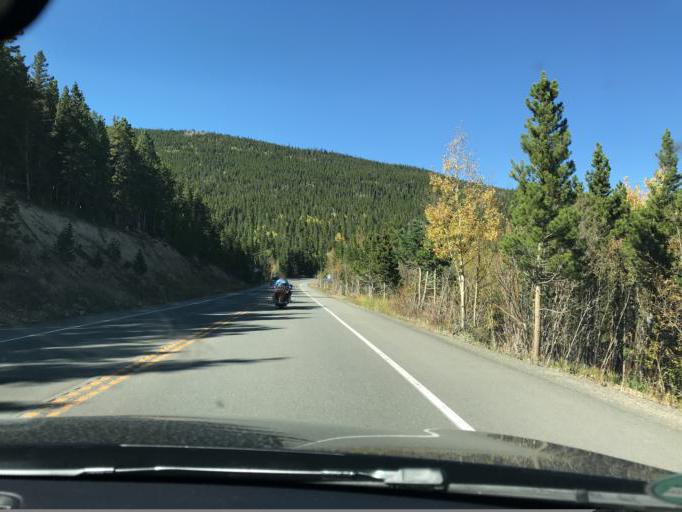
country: US
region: Colorado
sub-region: Boulder County
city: Nederland
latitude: 40.0568
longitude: -105.5231
